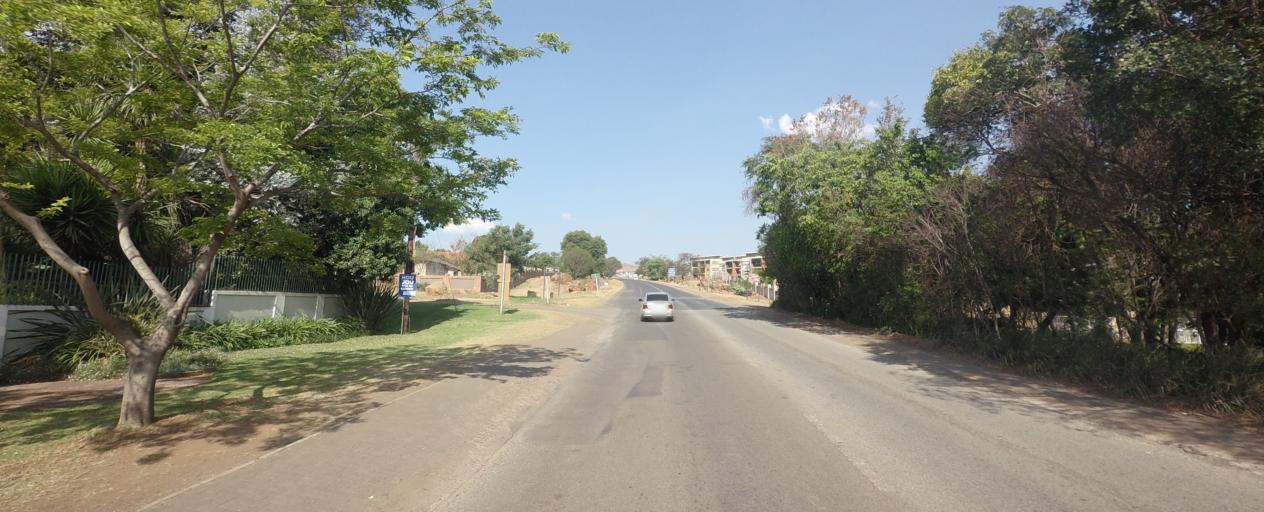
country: ZA
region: Mpumalanga
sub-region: Ehlanzeni District
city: Lydenburg
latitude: -25.1026
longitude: 30.4739
